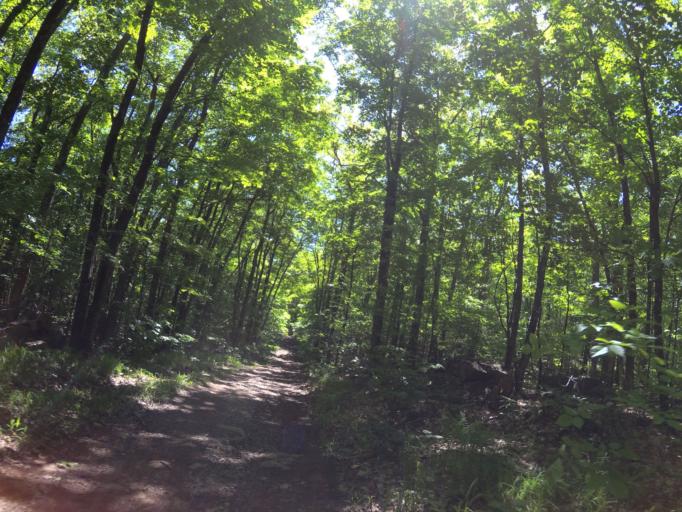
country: CA
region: Ontario
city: Renfrew
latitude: 45.0445
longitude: -77.0831
